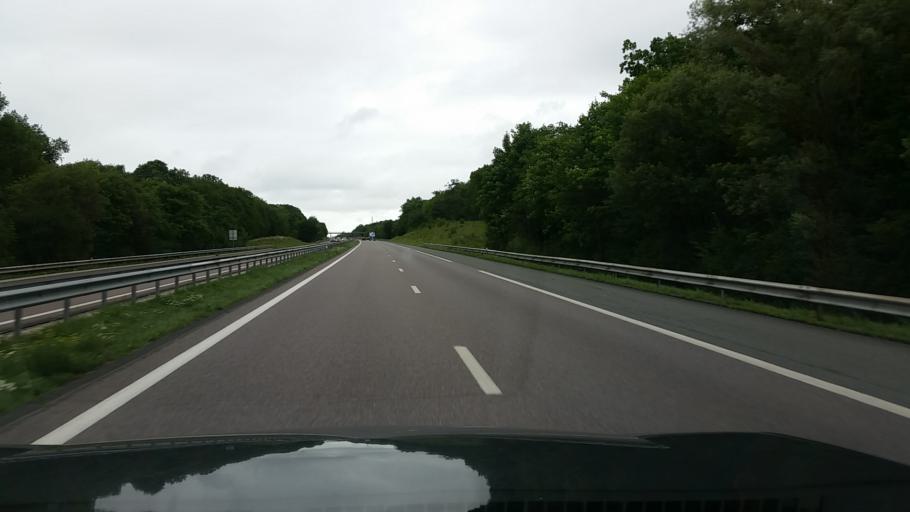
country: FR
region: Lorraine
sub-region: Departement de Meurthe-et-Moselle
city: Colombey-les-Belles
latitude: 48.4958
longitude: 5.9074
